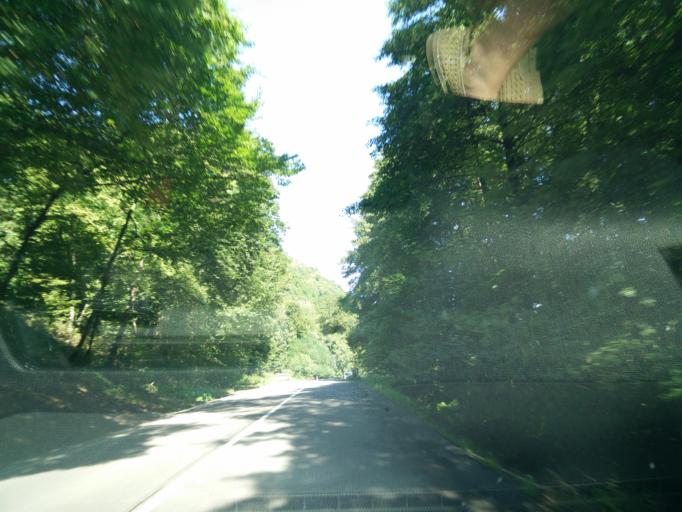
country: SK
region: Banskobystricky
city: Nova Bana
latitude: 48.4007
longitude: 18.6189
